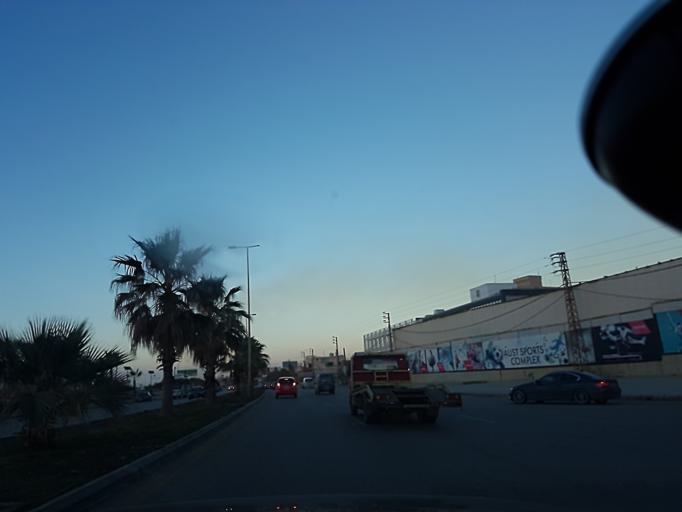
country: LB
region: Liban-Sud
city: Sidon
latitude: 33.5800
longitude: 35.3843
